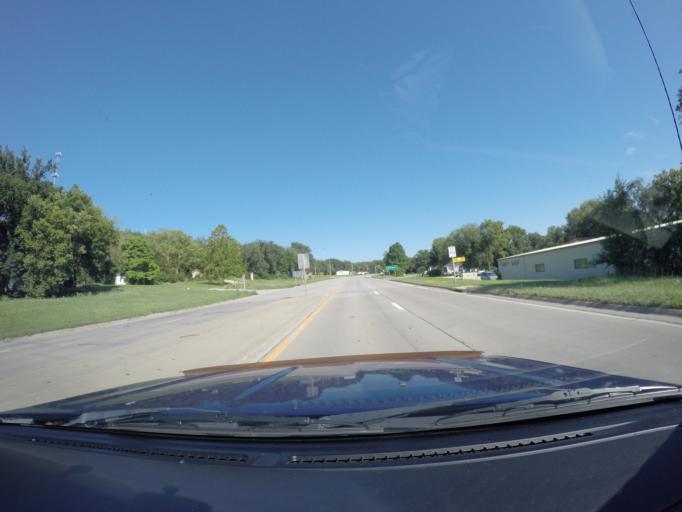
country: US
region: Kansas
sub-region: Riley County
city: Manhattan
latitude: 39.1718
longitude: -96.5455
